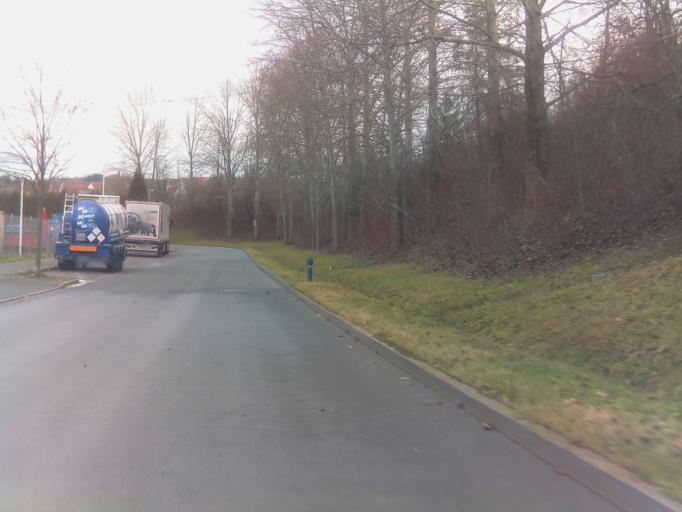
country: DE
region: Thuringia
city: Unterwellenborn
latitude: 50.6509
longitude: 11.4318
